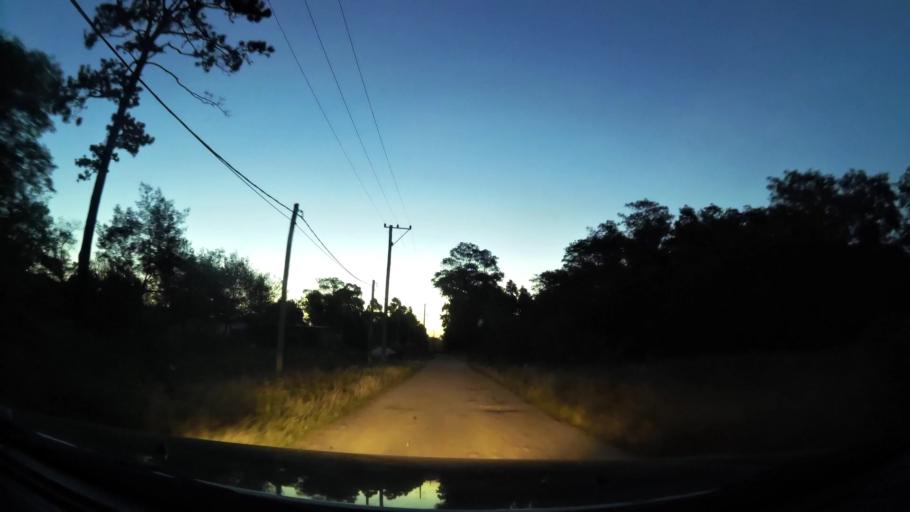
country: UY
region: Canelones
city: Atlantida
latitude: -34.7624
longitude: -55.7574
